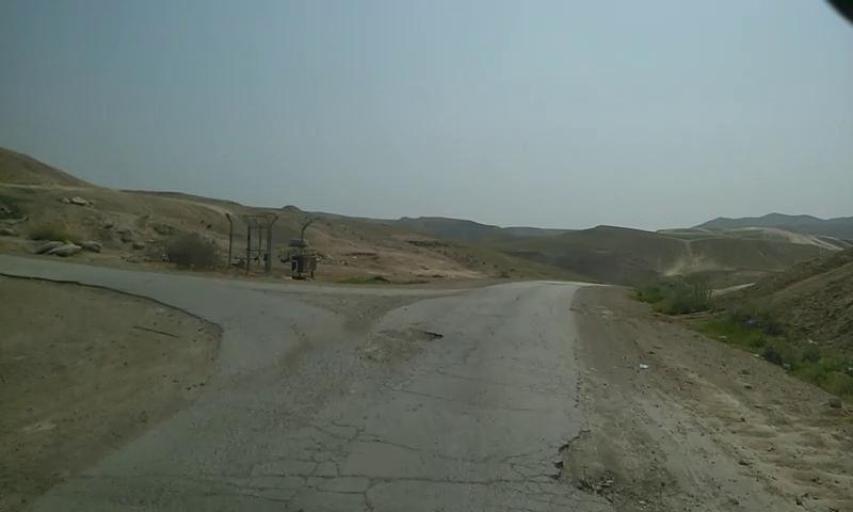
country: PS
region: West Bank
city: Jericho
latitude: 31.7863
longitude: 35.4300
